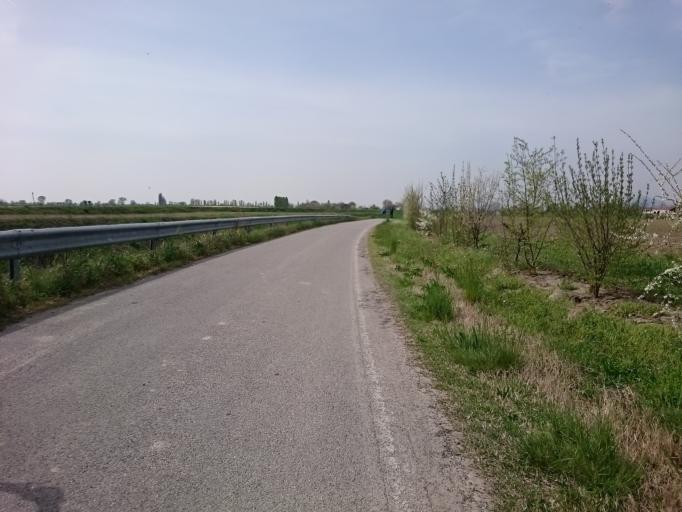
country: IT
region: Veneto
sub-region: Provincia di Padova
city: Tribano
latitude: 45.1877
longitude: 11.8337
